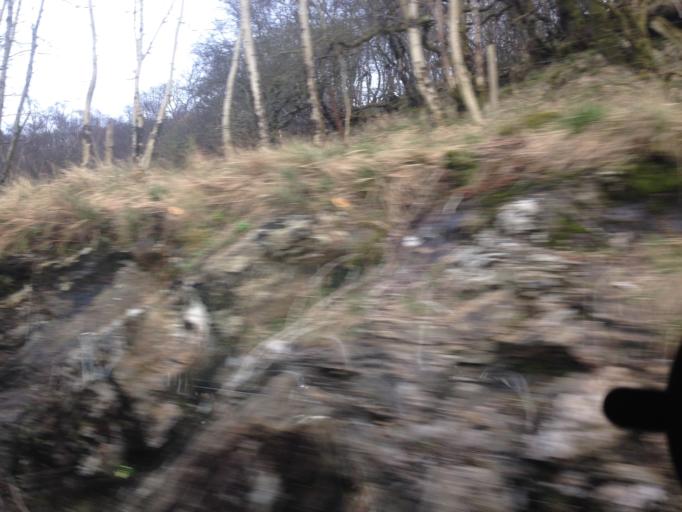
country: GB
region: Scotland
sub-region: Argyll and Bute
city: Garelochhead
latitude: 56.1679
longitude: -4.7812
